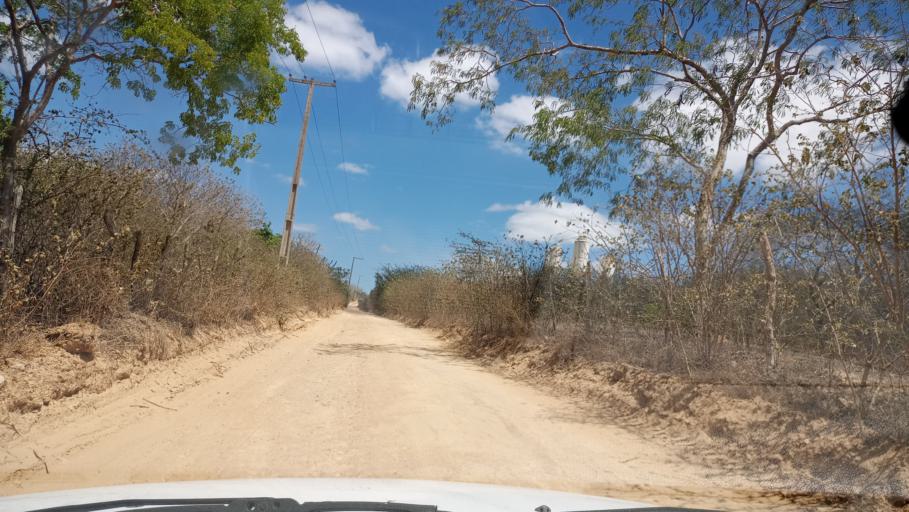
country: BR
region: Rio Grande do Norte
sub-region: Sao Paulo Do Potengi
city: Sao Paulo do Potengi
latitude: -5.7923
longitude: -35.9197
